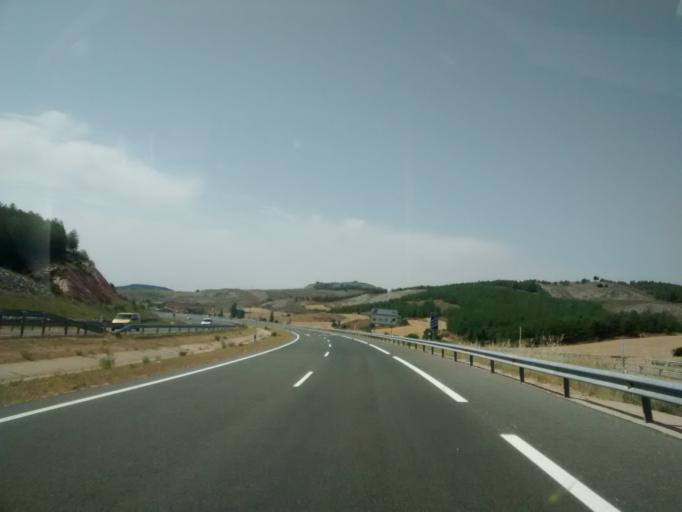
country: ES
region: Castille and Leon
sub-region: Provincia de Palencia
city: Alar del Rey
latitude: 42.7251
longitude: -4.2901
